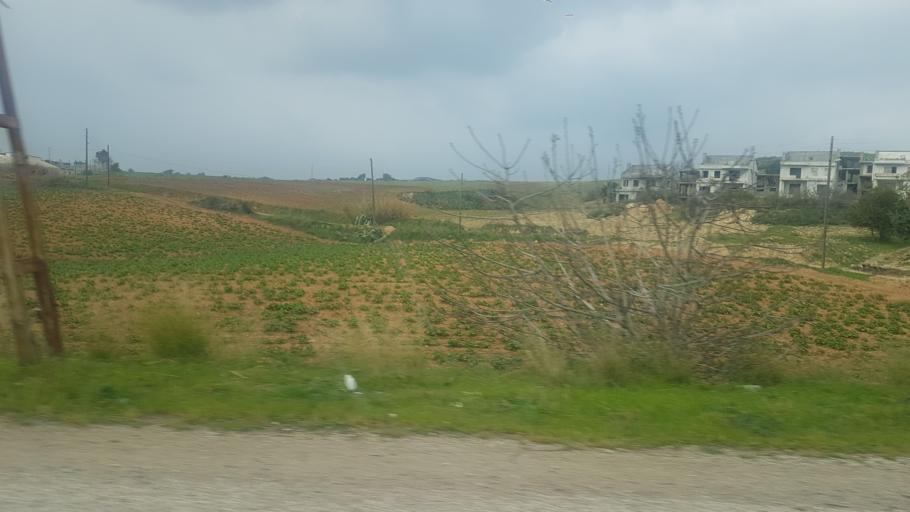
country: TR
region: Adana
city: Seyhan
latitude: 37.0551
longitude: 35.2188
